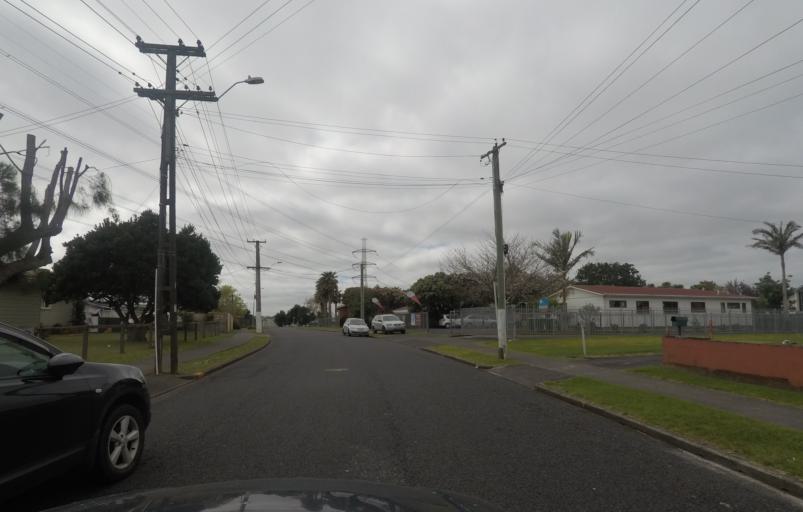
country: NZ
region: Auckland
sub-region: Auckland
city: Manukau City
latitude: -36.9617
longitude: 174.8682
